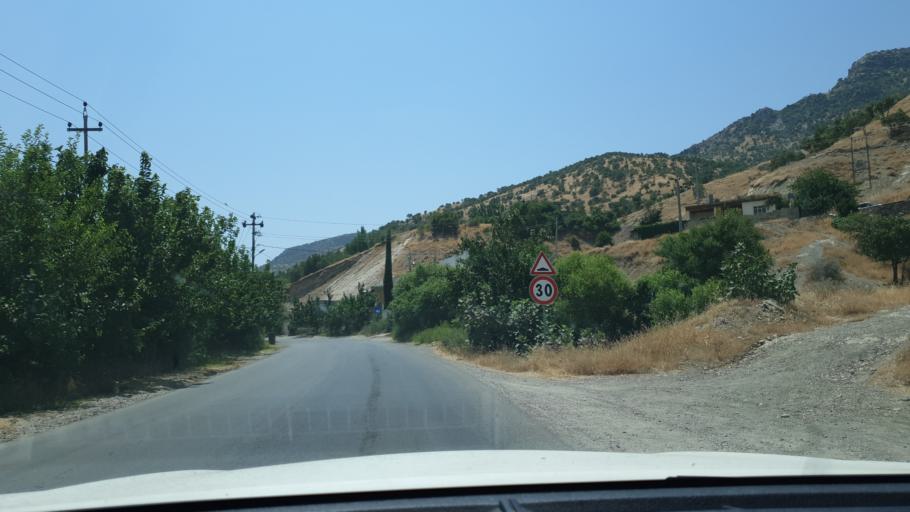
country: IQ
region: Arbil
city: Nahiyat Hiran
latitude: 36.2874
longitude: 44.4855
